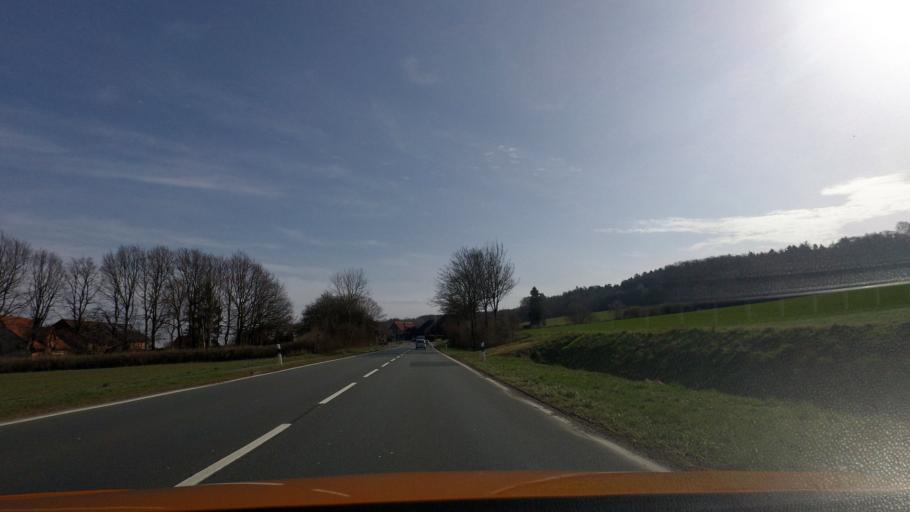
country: DE
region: Lower Saxony
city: Heuerssen
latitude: 52.3370
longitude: 9.2941
